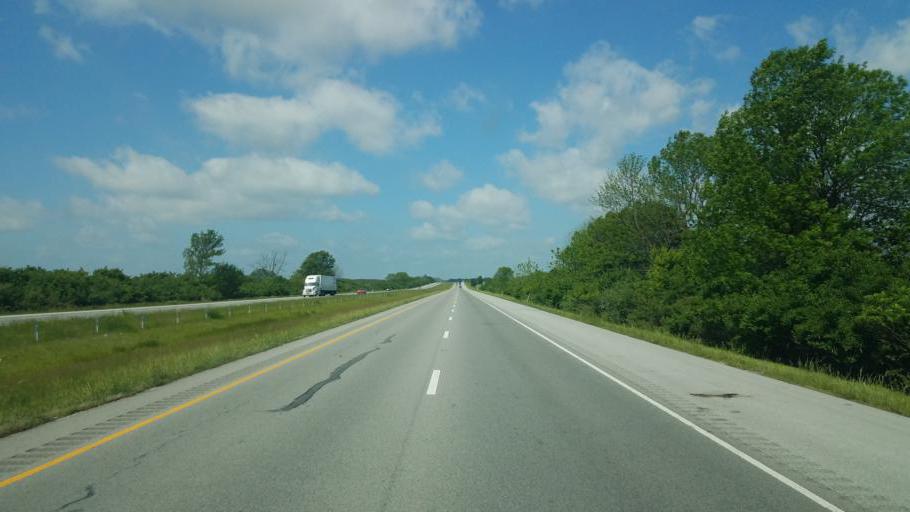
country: US
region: Indiana
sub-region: Putnam County
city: Cloverdale
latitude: 39.5558
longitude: -86.6850
